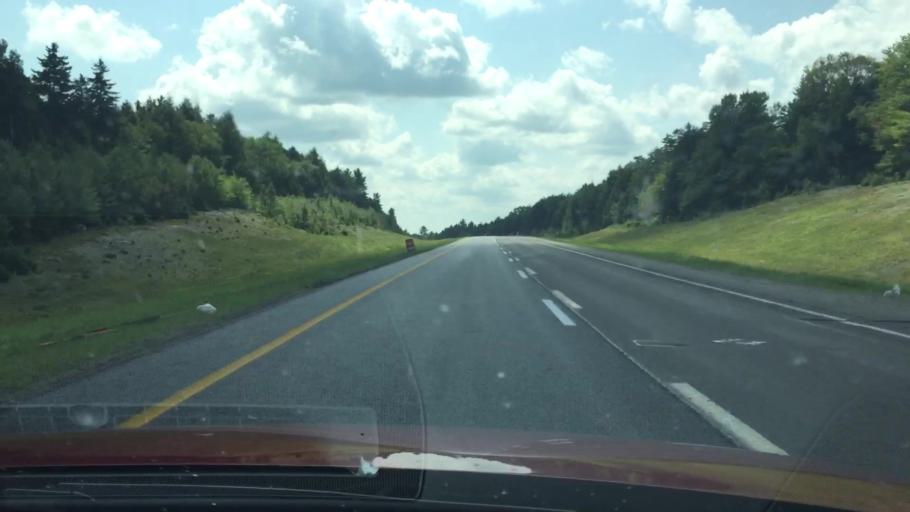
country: US
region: Maine
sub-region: Penobscot County
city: Medway
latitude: 45.6795
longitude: -68.4947
